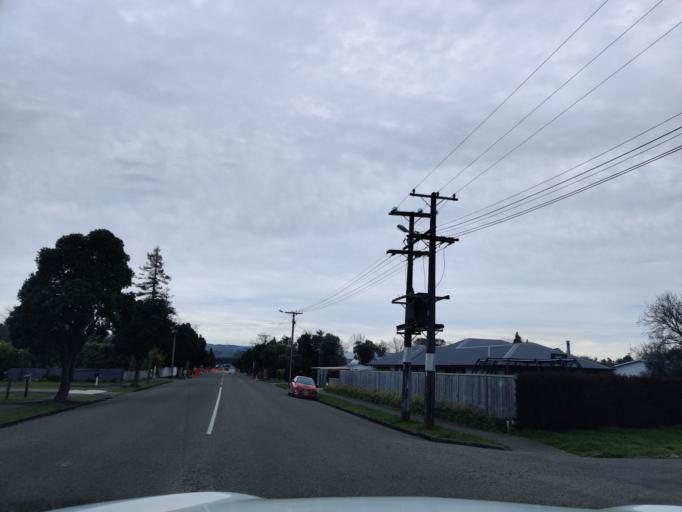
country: NZ
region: Manawatu-Wanganui
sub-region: Palmerston North City
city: Palmerston North
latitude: -40.2854
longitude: 175.7558
